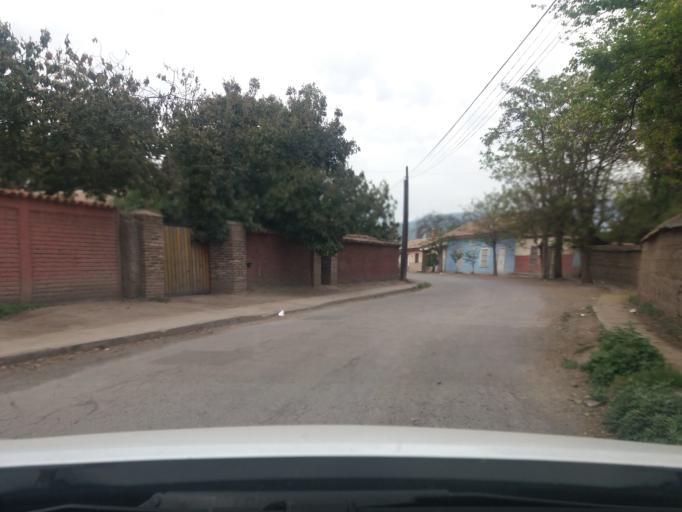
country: CL
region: Valparaiso
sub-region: Provincia de Los Andes
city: Los Andes
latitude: -32.8444
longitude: -70.6324
